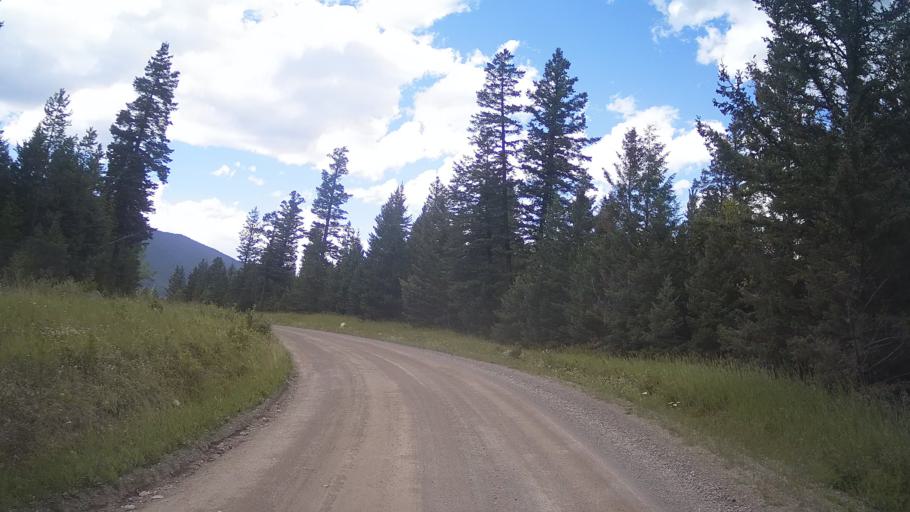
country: CA
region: British Columbia
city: Lillooet
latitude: 51.3122
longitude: -121.8493
